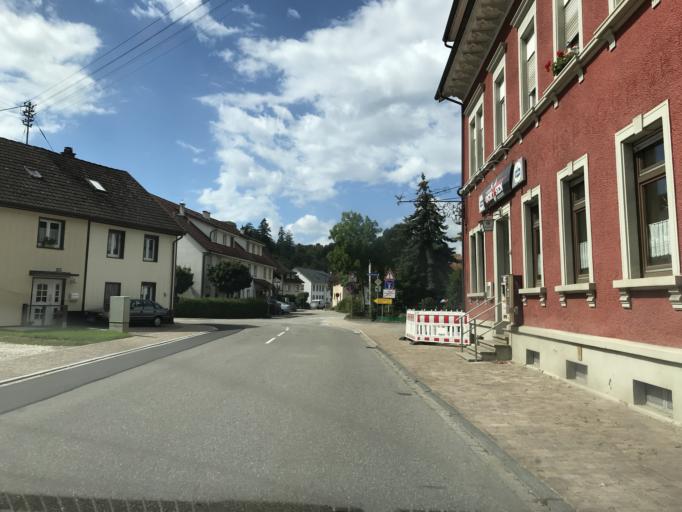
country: DE
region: Baden-Wuerttemberg
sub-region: Freiburg Region
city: Maulburg
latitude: 47.6411
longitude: 7.7785
